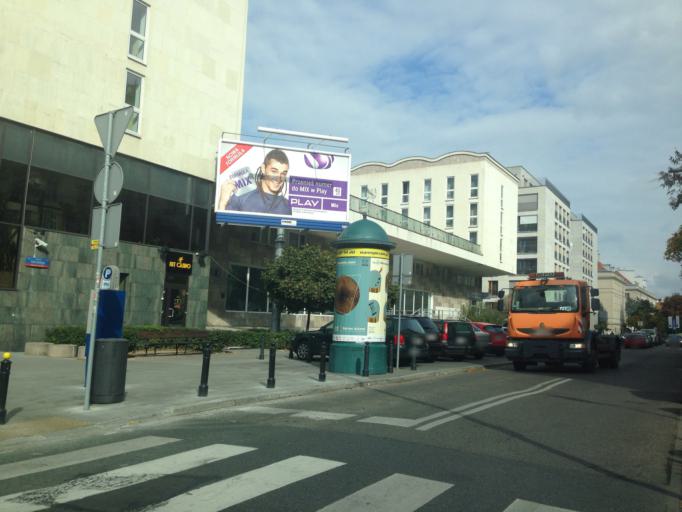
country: PL
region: Masovian Voivodeship
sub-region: Warszawa
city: Warsaw
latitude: 52.2334
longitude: 21.0145
